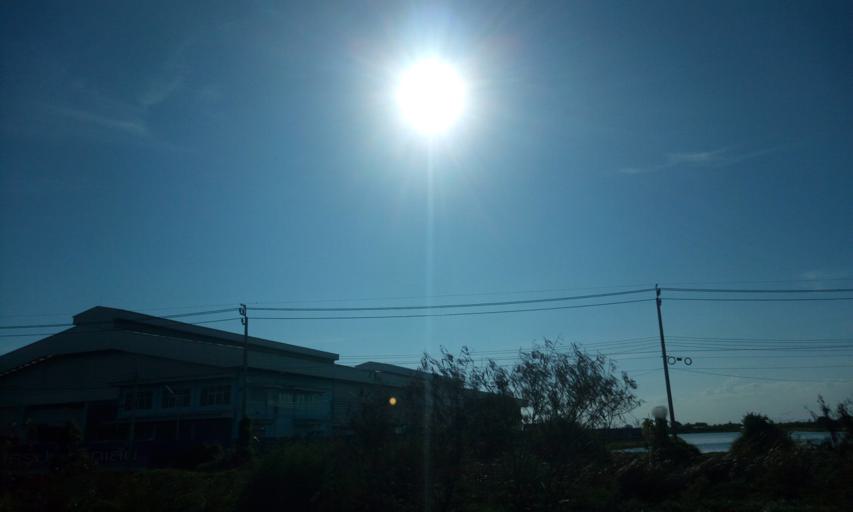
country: TH
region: Samut Prakan
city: Bang Bo District
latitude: 13.5408
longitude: 100.7506
